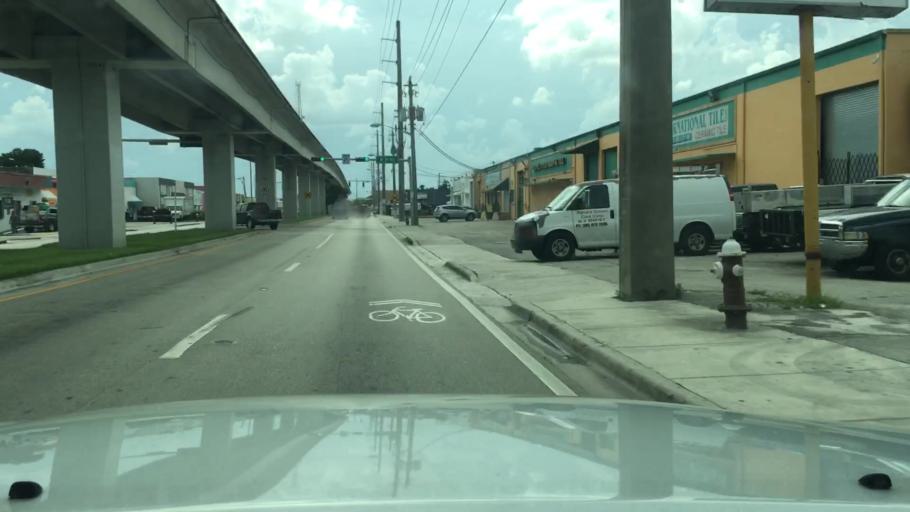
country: US
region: Florida
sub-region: Miami-Dade County
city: Hialeah
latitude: 25.8408
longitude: -80.2852
